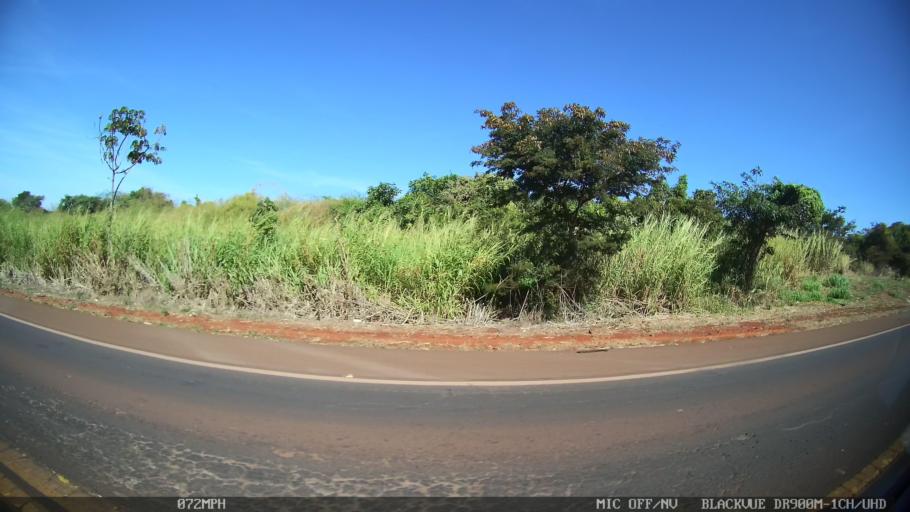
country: BR
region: Sao Paulo
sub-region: Ipua
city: Ipua
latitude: -20.4936
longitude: -48.0319
